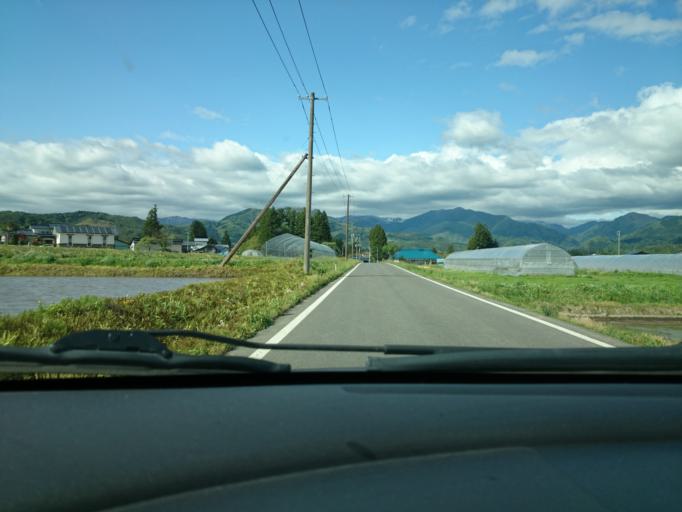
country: JP
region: Fukushima
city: Kitakata
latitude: 37.6974
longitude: 139.8443
